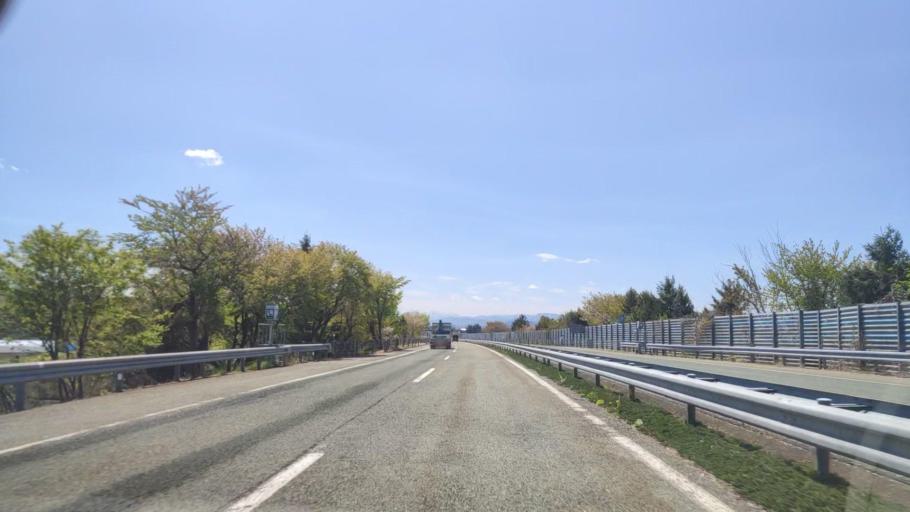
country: JP
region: Akita
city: Yokotemachi
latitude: 39.3143
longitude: 140.5158
